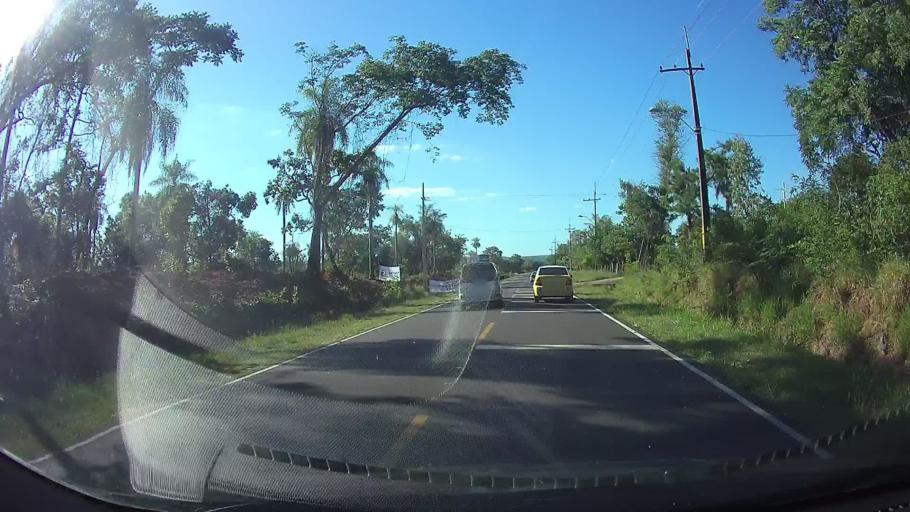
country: PY
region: Cordillera
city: Atyra
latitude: -25.3021
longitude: -57.1597
